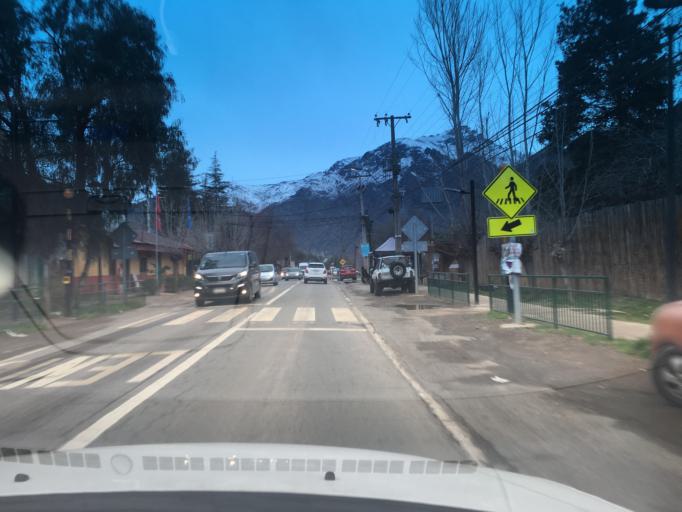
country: CL
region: Santiago Metropolitan
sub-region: Provincia de Cordillera
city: Puente Alto
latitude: -33.6944
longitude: -70.3352
